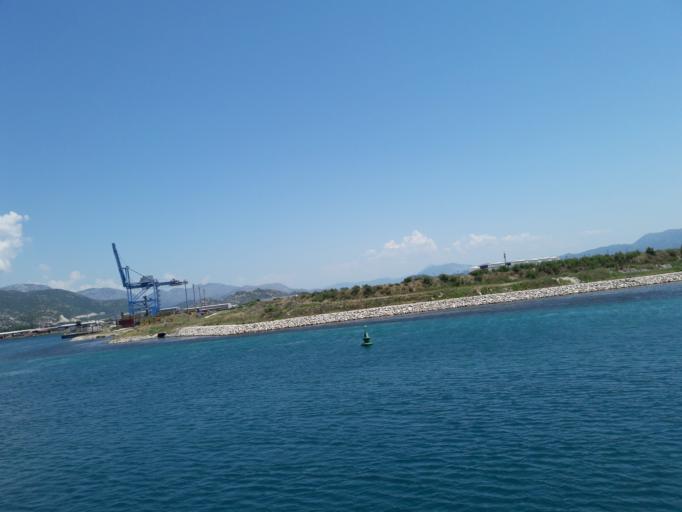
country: HR
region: Dubrovacko-Neretvanska
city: Komin
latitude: 43.0427
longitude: 17.4204
